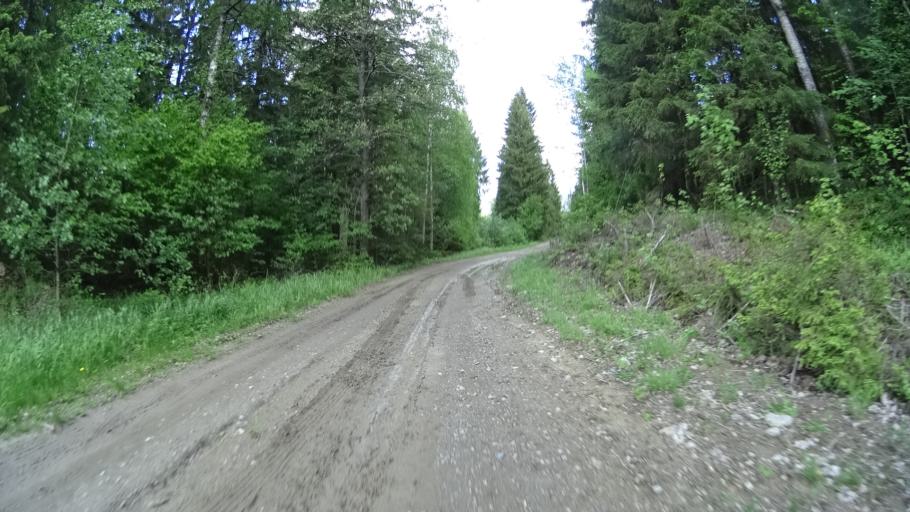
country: FI
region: Uusimaa
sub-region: Raaseporin
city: Karis
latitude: 60.1490
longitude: 23.6237
